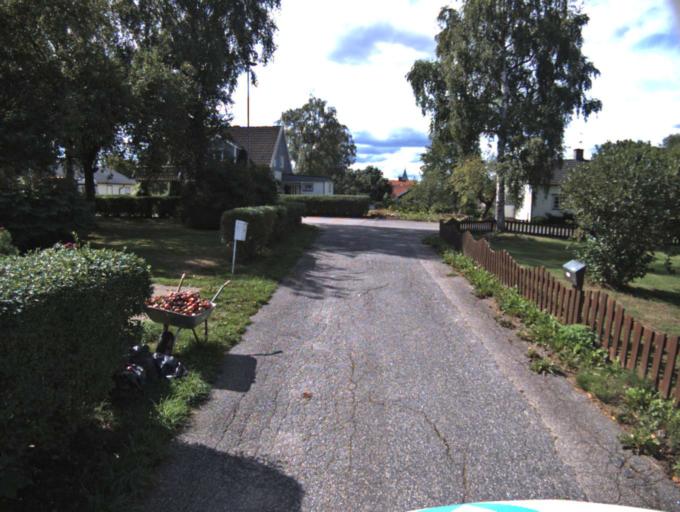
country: SE
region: Vaestra Goetaland
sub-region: Ulricehamns Kommun
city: Ulricehamn
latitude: 57.8995
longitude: 13.4627
